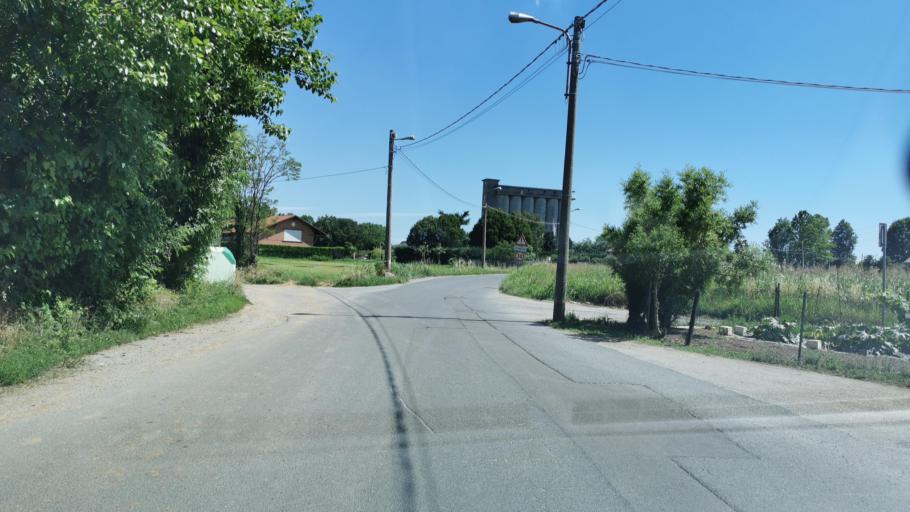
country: IT
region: Piedmont
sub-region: Provincia di Torino
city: Druento
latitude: 45.1184
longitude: 7.5630
